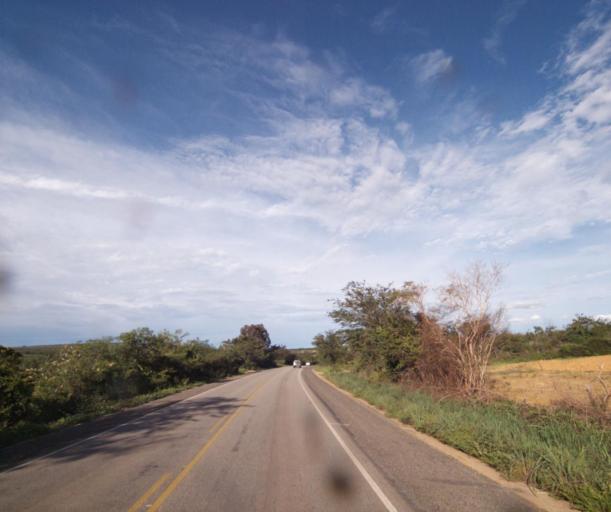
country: BR
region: Bahia
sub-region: Caetite
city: Caetite
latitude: -14.0862
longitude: -42.5675
